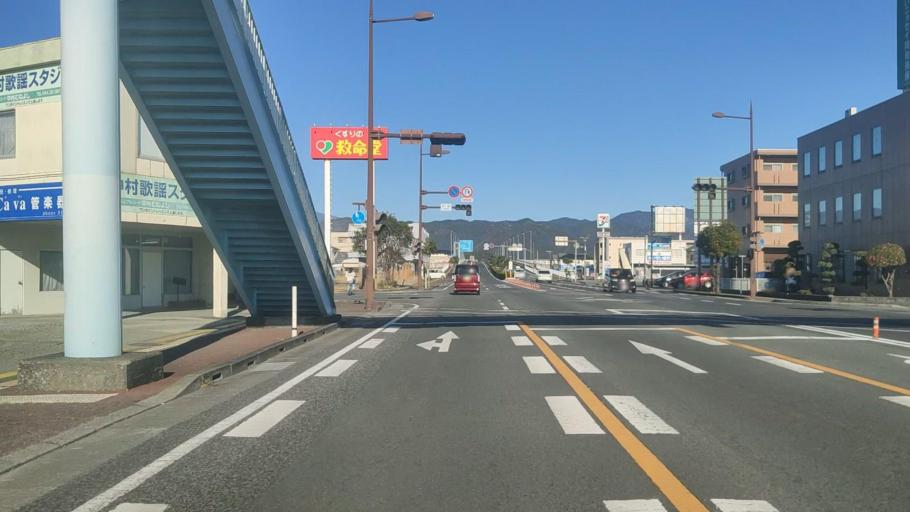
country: JP
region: Miyazaki
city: Nobeoka
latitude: 32.5792
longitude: 131.6827
